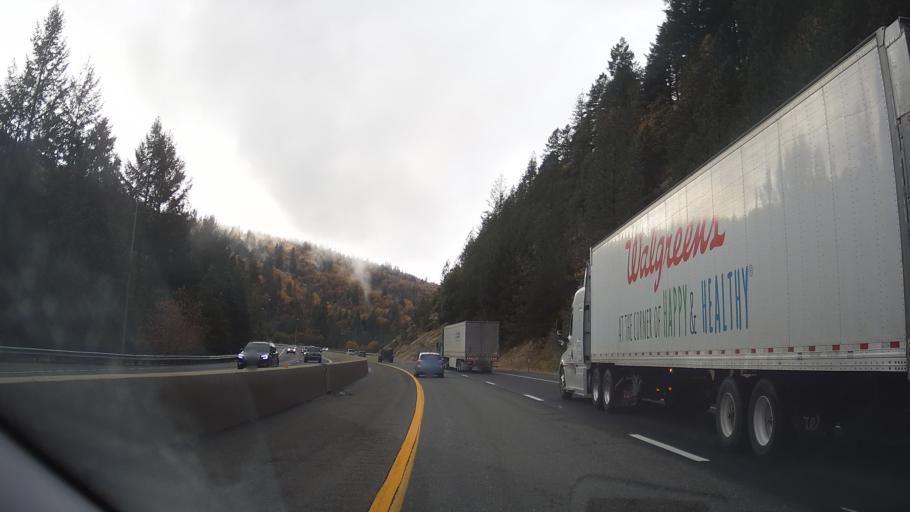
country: US
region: California
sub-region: Placer County
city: Colfax
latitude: 39.1956
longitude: -120.8167
